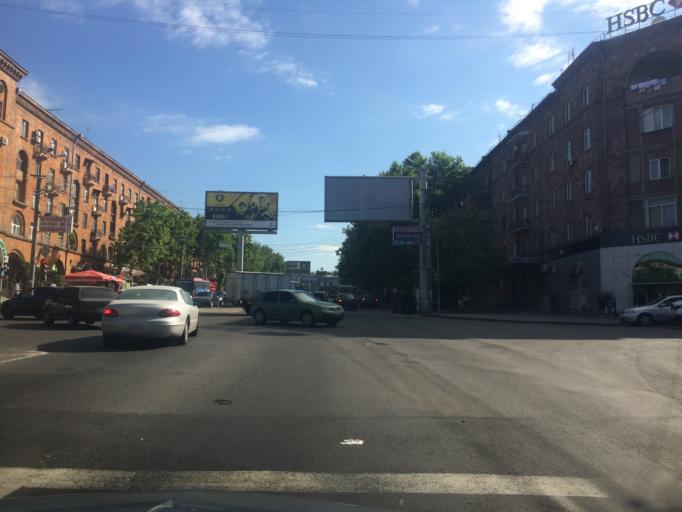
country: AM
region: Yerevan
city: Yerevan
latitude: 40.2073
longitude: 44.5275
